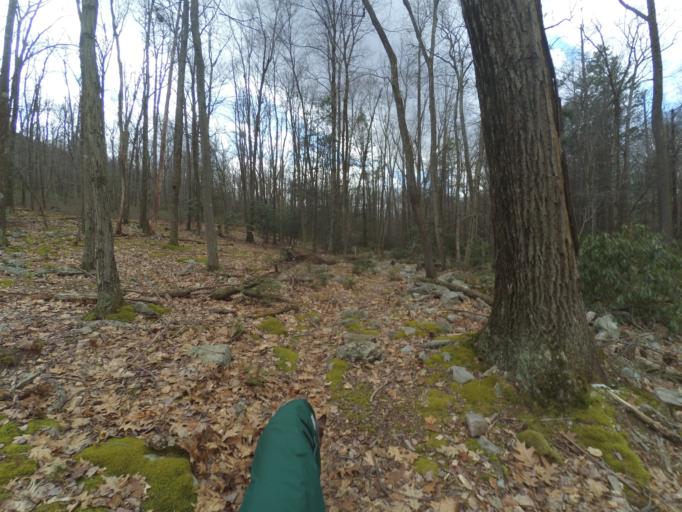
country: US
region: Pennsylvania
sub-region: Centre County
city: Boalsburg
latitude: 40.7426
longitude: -77.7257
